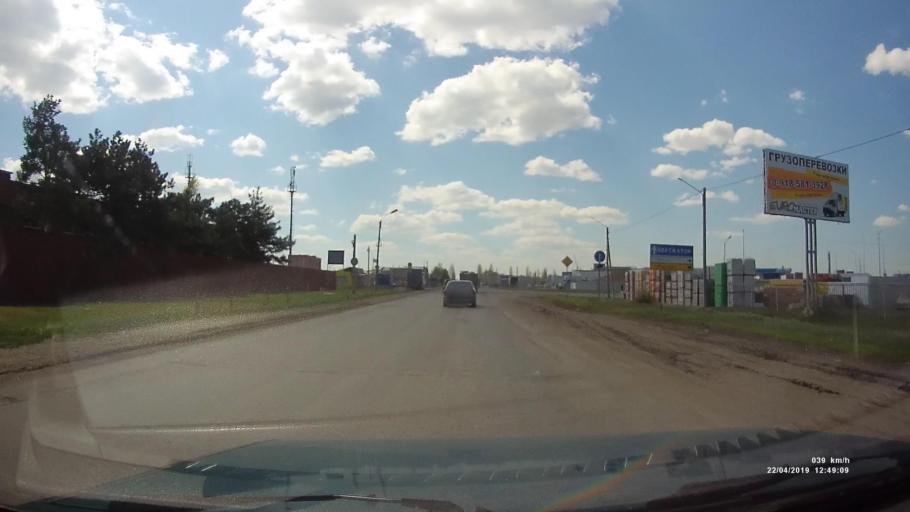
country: RU
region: Rostov
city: Azov
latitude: 47.0934
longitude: 39.3989
